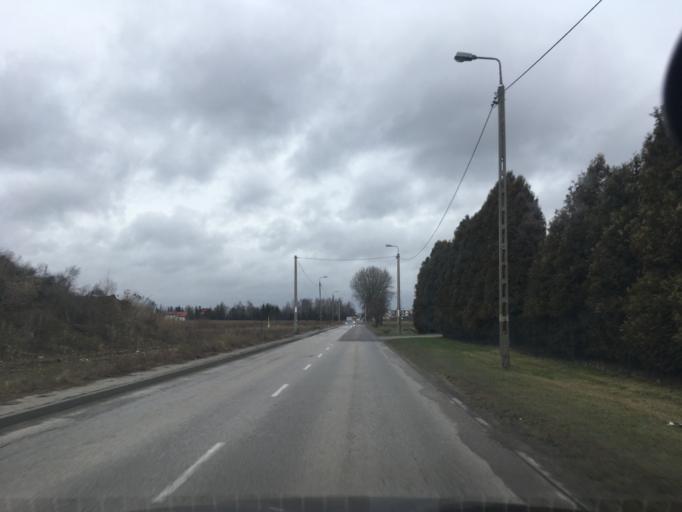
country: PL
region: Masovian Voivodeship
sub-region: Powiat piaseczynski
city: Lesznowola
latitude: 52.0964
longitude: 20.9335
